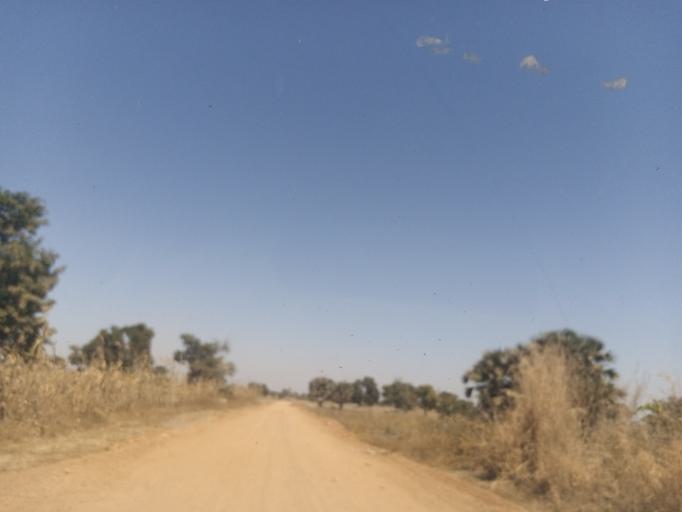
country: NG
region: Adamawa
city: Yola
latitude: 9.2901
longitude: 12.8851
